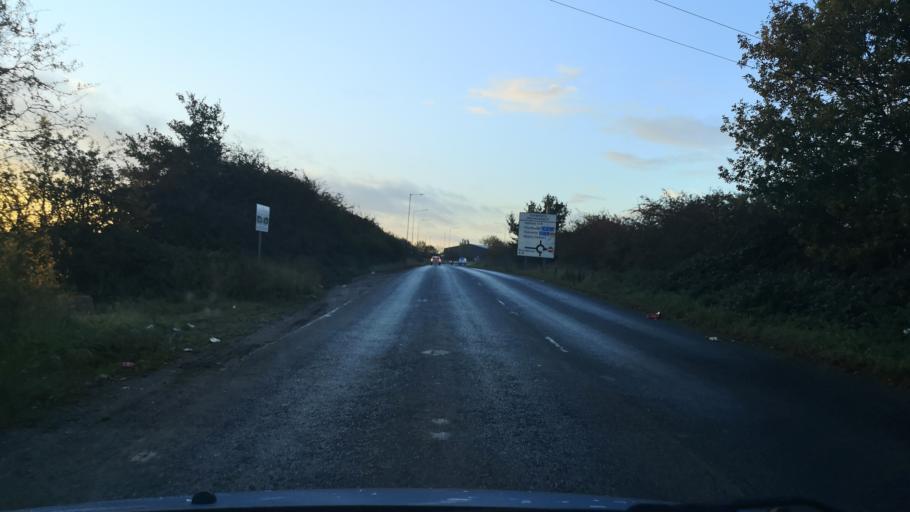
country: GB
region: England
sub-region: Doncaster
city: Hatfield
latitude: 53.5948
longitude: -0.9631
